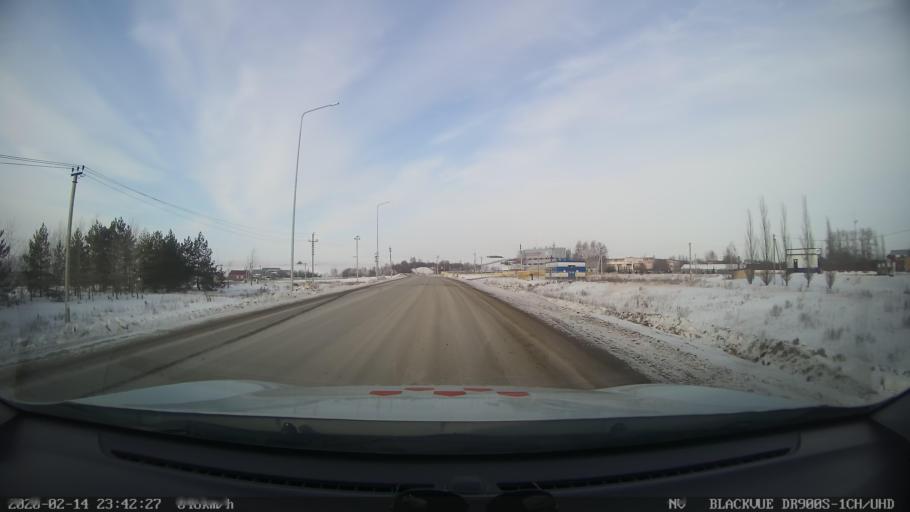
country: RU
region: Tatarstan
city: Kuybyshevskiy Zaton
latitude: 55.1918
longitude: 49.2471
